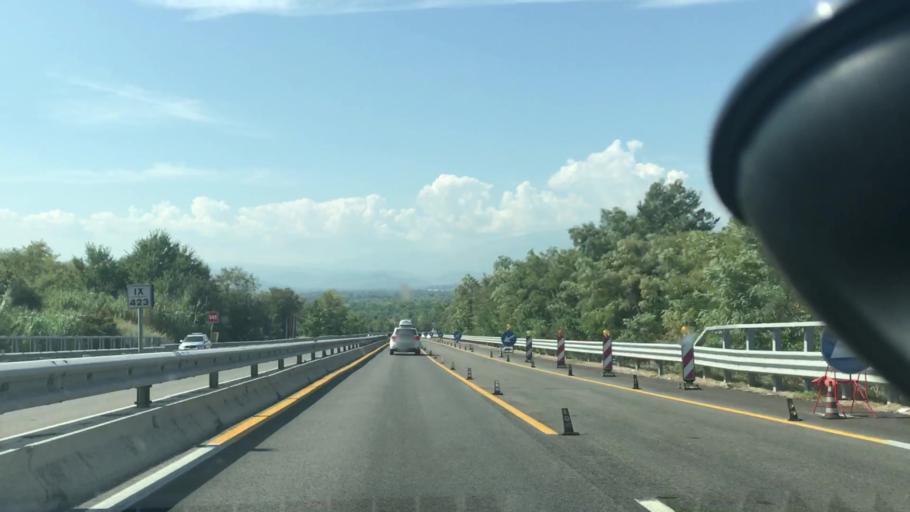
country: IT
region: Abruzzo
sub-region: Provincia di Chieti
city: Torino di Sangro
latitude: 42.2012
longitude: 14.5166
